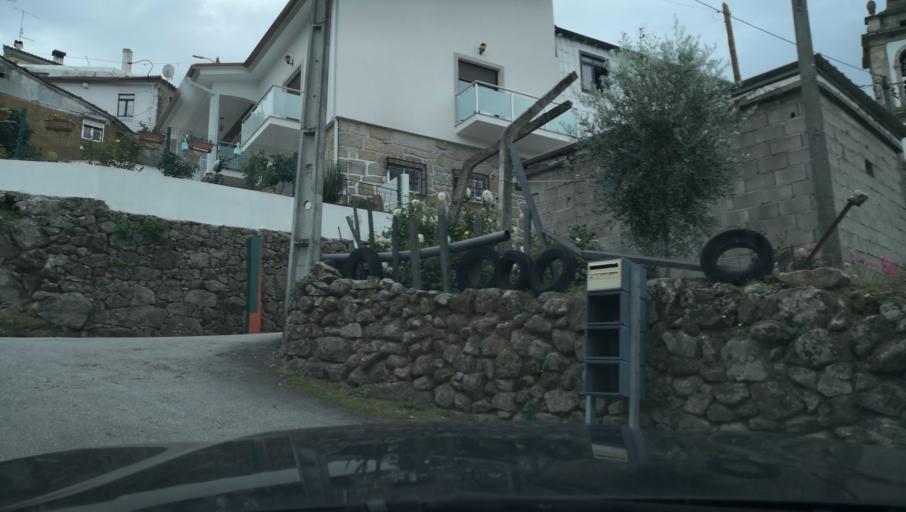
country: PT
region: Vila Real
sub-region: Vila Real
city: Vila Real
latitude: 41.2858
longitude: -7.7617
